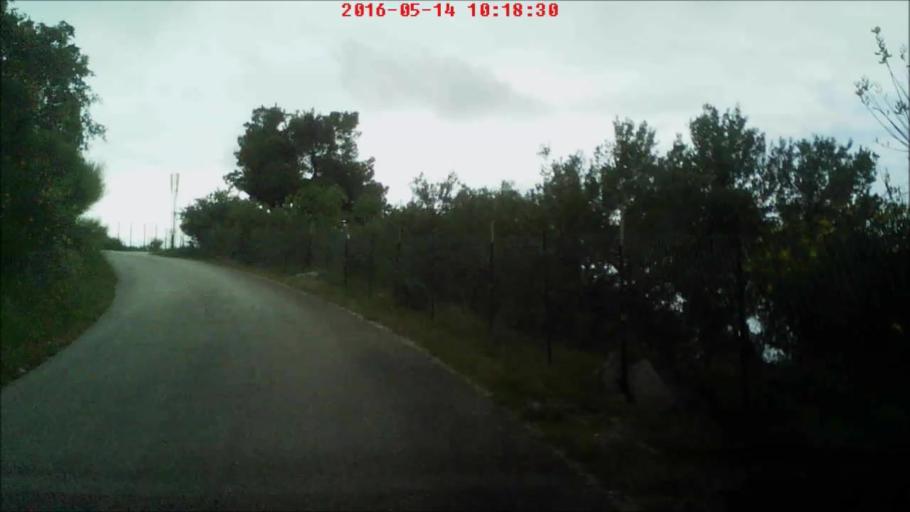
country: HR
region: Dubrovacko-Neretvanska
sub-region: Grad Dubrovnik
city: Mokosica
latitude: 42.7190
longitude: 17.9676
